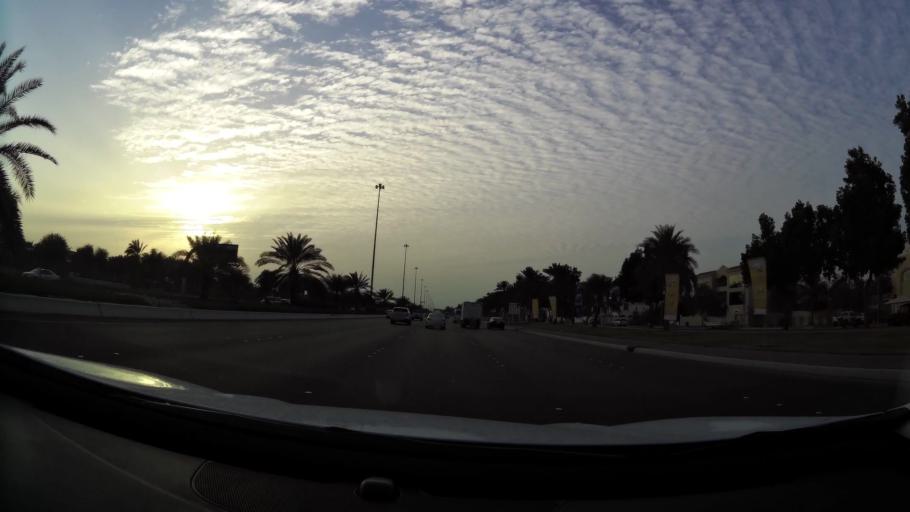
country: AE
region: Abu Dhabi
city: Abu Dhabi
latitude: 24.4240
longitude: 54.4127
